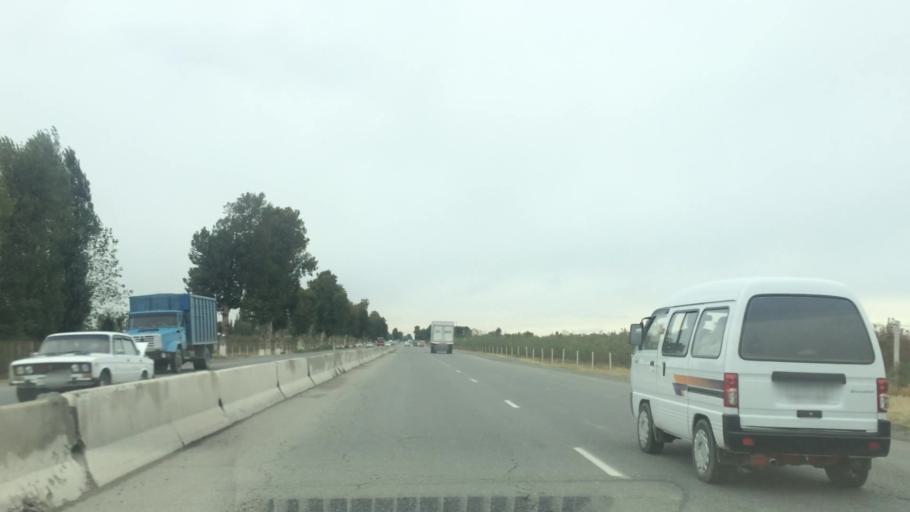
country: UZ
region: Samarqand
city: Jomboy
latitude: 39.7343
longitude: 67.1665
